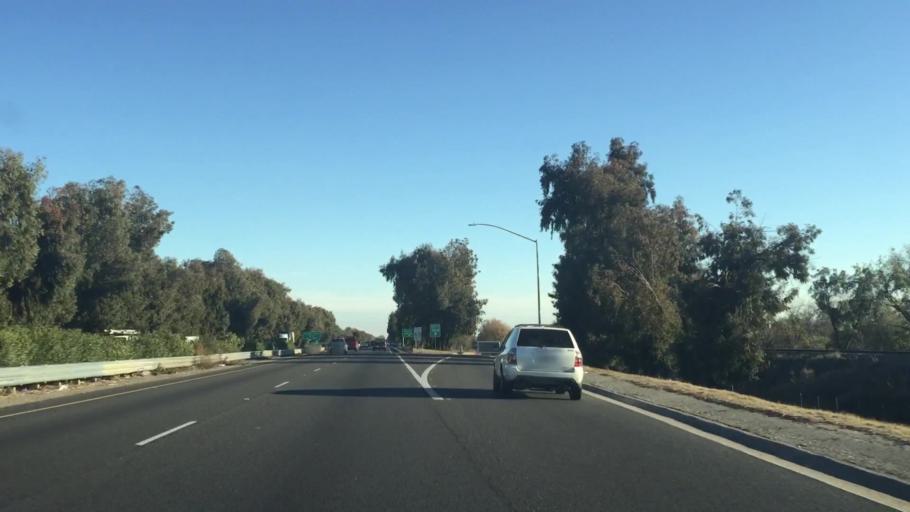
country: US
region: California
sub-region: Yuba County
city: Marysville
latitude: 39.1280
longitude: -121.5832
